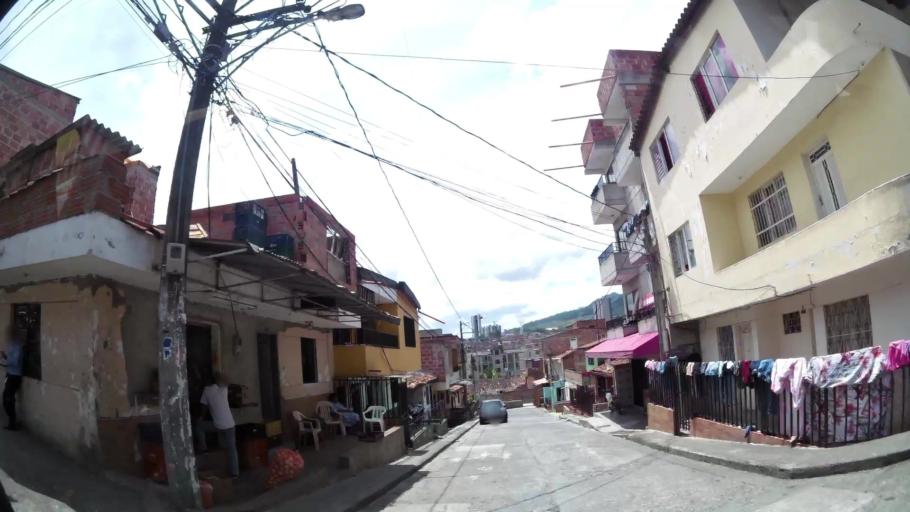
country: CO
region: Antioquia
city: Bello
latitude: 6.3471
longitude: -75.5626
